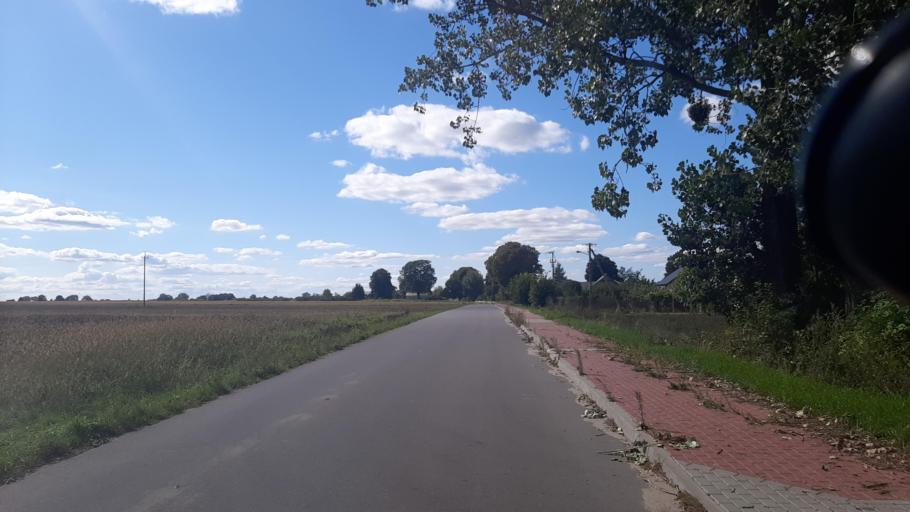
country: PL
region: Lublin Voivodeship
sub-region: Powiat lubelski
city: Garbow
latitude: 51.4028
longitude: 22.3494
